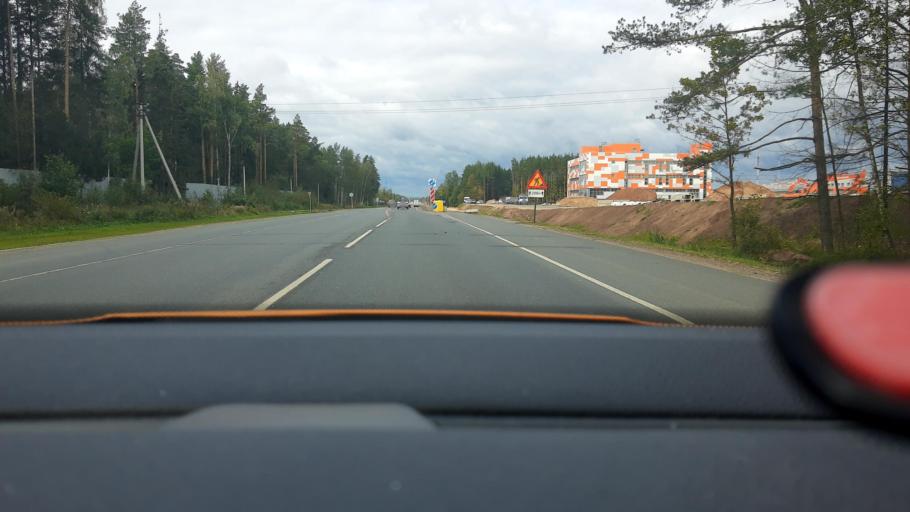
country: RU
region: Moskovskaya
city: Zelenogradskiy
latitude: 56.1020
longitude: 37.9682
